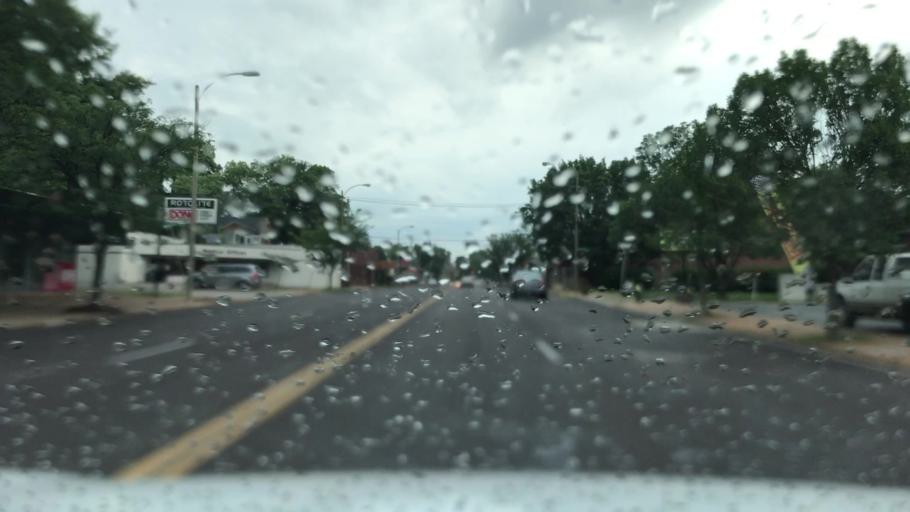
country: US
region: Missouri
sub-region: Saint Louis County
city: Maplewood
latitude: 38.5841
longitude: -90.2930
